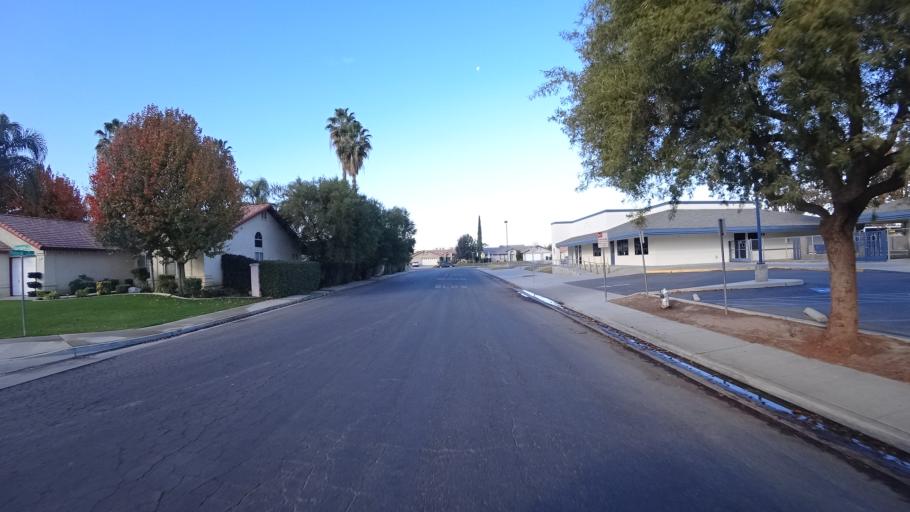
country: US
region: California
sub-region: Kern County
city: Rosedale
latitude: 35.3489
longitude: -119.1615
